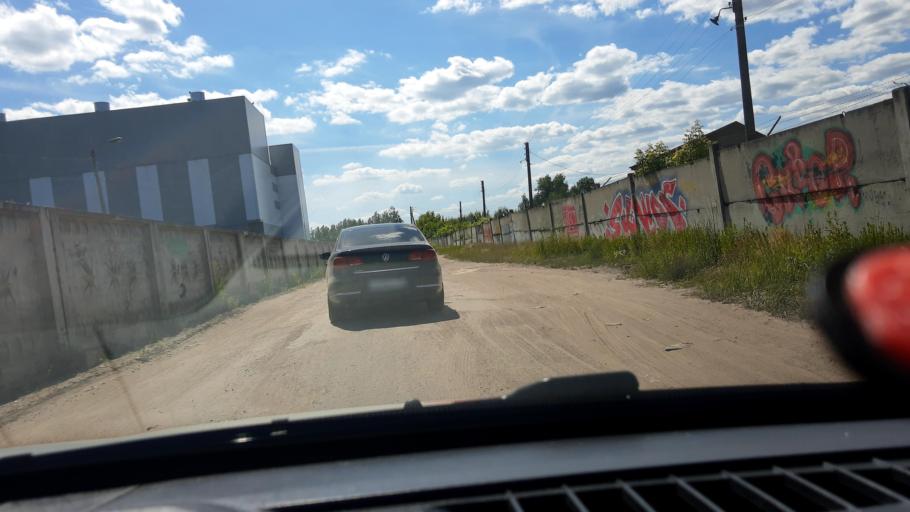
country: RU
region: Nizjnij Novgorod
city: Gorbatovka
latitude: 56.3040
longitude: 43.8124
